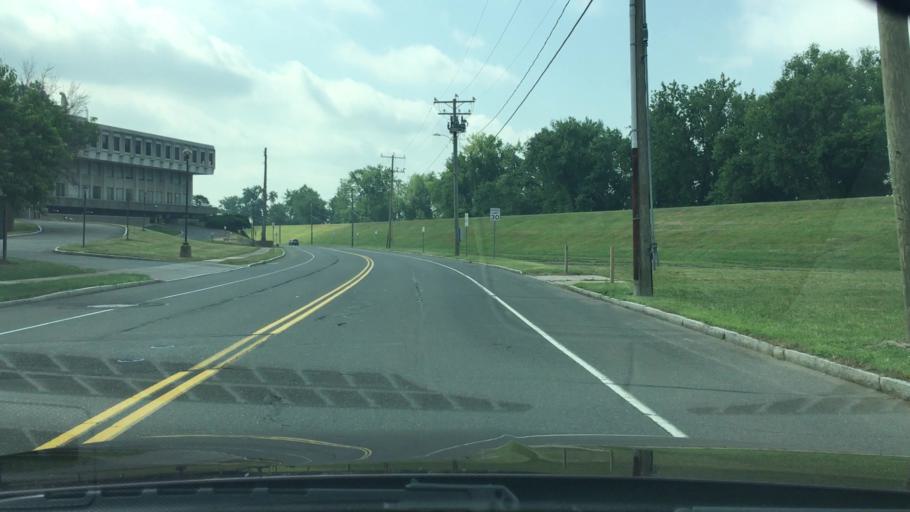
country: US
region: Connecticut
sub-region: Hartford County
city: Hartford
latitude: 41.7646
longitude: -72.6628
